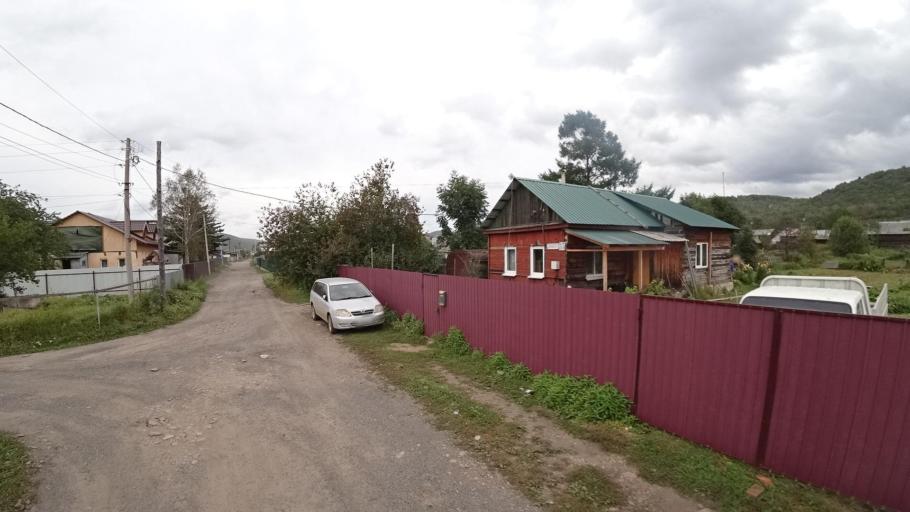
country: RU
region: Jewish Autonomous Oblast
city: Khingansk
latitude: 49.0056
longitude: 131.0517
